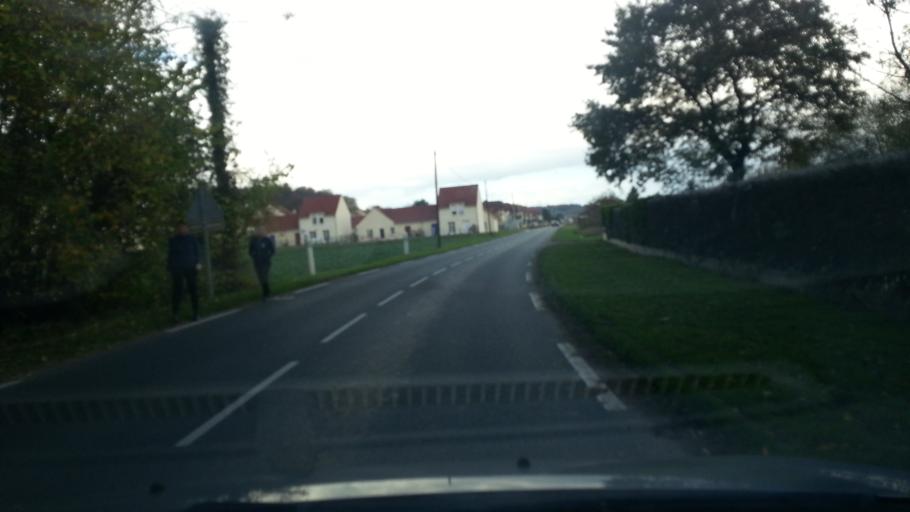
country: FR
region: Picardie
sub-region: Departement de l'Oise
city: Balagny-sur-Therain
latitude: 49.2867
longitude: 2.3449
